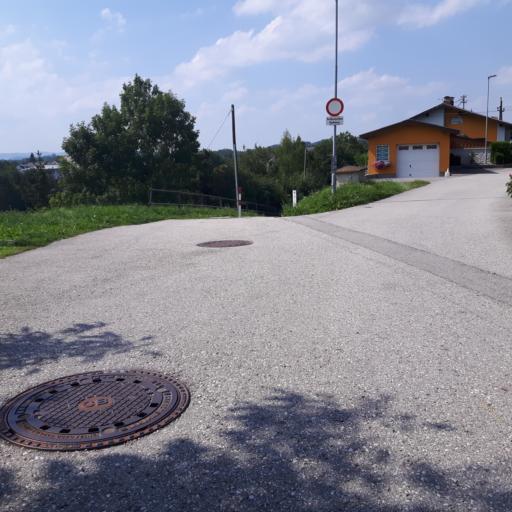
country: AT
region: Upper Austria
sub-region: Wels-Land
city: Stadl-Paura
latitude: 48.0815
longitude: 13.8690
